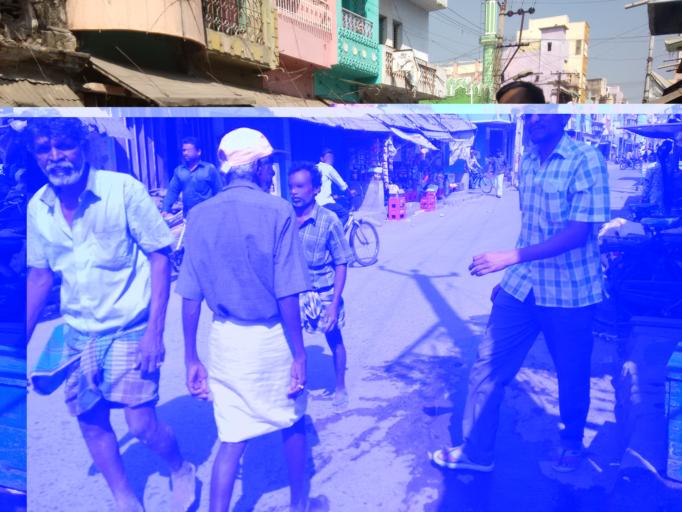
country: IN
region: Andhra Pradesh
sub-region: Chittoor
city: Chittoor
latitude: 13.2186
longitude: 79.0950
